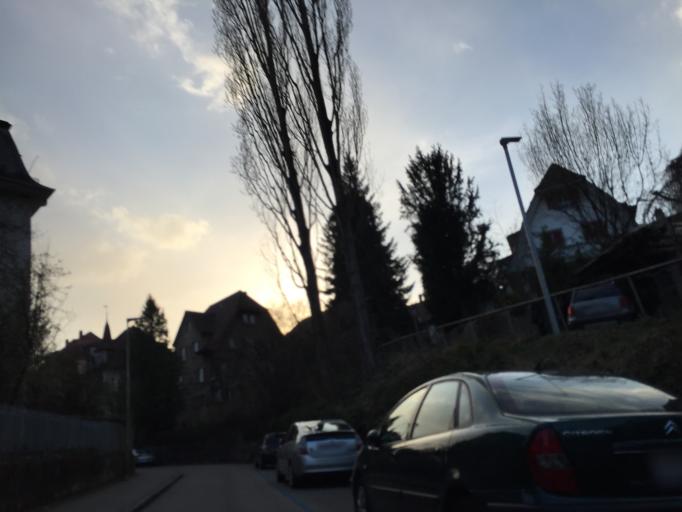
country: CH
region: Bern
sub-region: Bern-Mittelland District
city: Koniz
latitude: 46.9418
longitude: 7.4253
